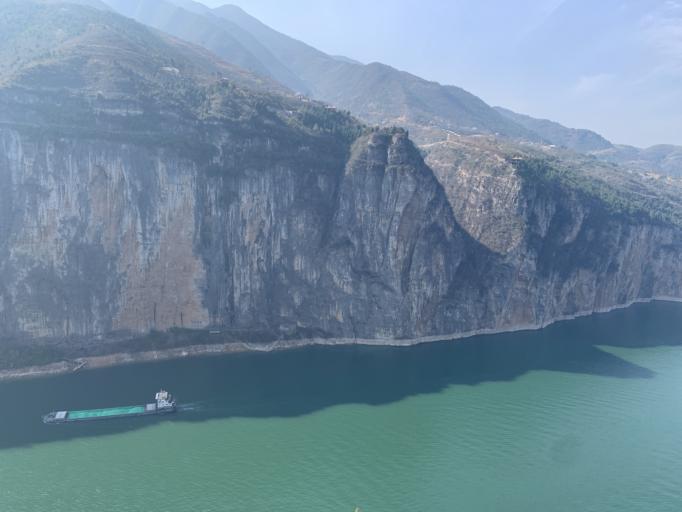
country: CN
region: Chongqing Shi
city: Baidi
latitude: 31.0406
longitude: 109.5869
